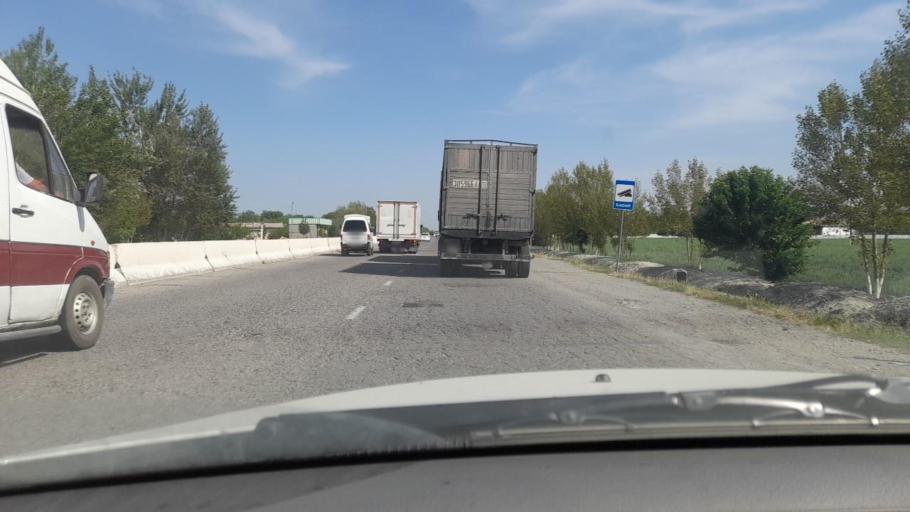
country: UZ
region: Samarqand
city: Chelak
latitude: 39.8519
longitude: 66.7993
